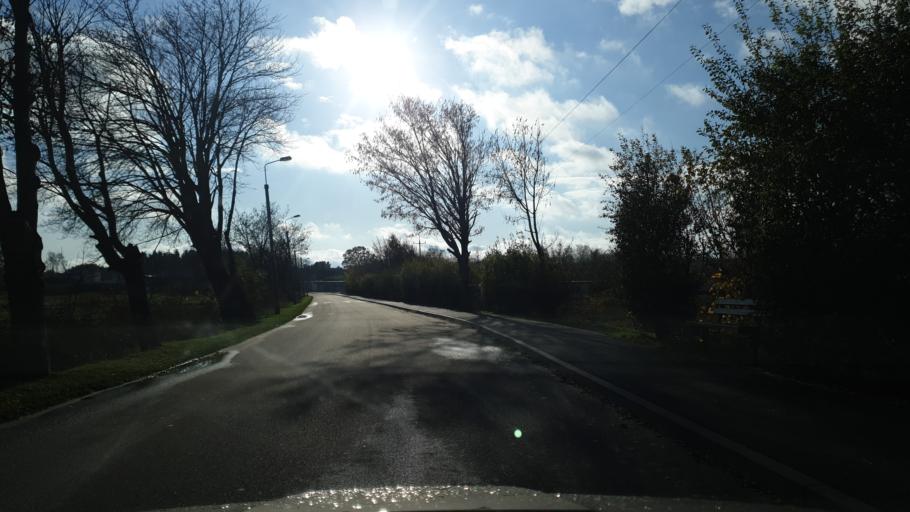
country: PL
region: Pomeranian Voivodeship
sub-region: Powiat pucki
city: Jastrzebia Gora
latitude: 54.8277
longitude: 18.2441
